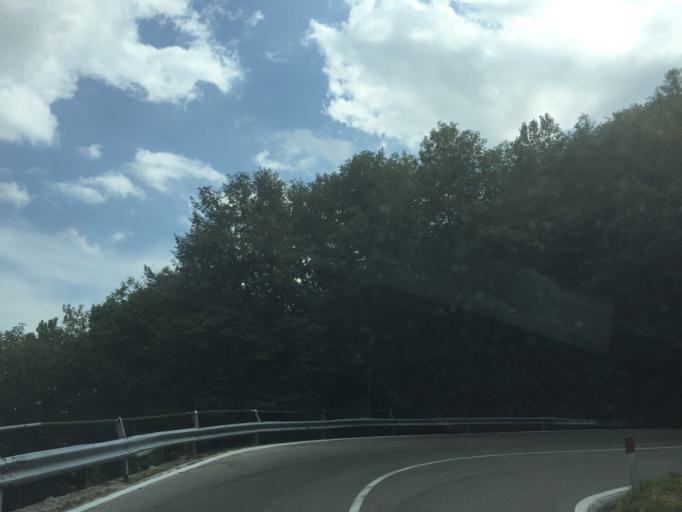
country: IT
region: Tuscany
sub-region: Provincia di Pistoia
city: Cutigliano
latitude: 44.1150
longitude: 10.7327
